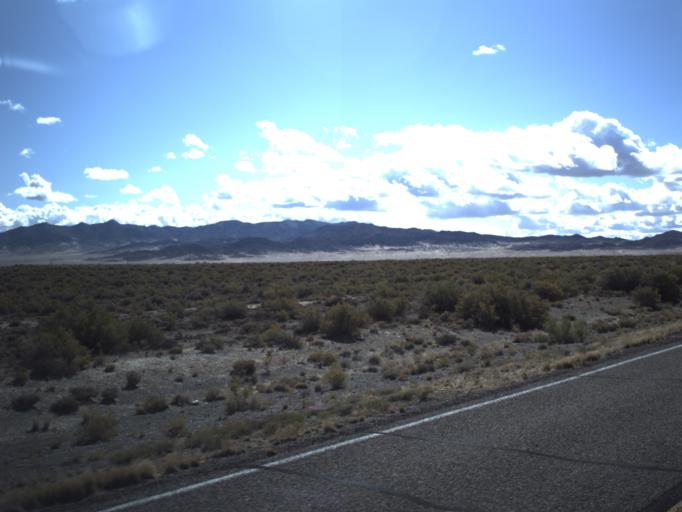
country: US
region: Nevada
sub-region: White Pine County
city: McGill
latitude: 39.0102
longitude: -114.0351
